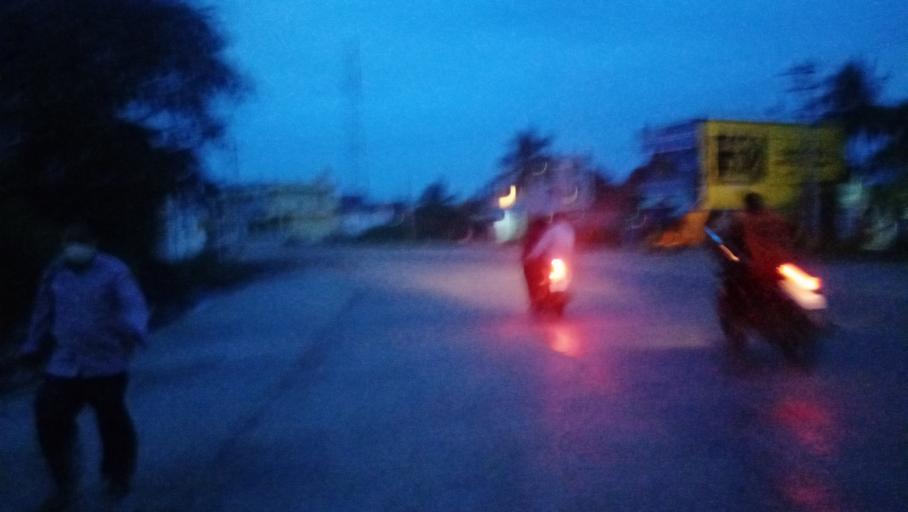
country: IN
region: Karnataka
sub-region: Tumkur
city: Pavagada
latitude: 13.9400
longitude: 77.2772
